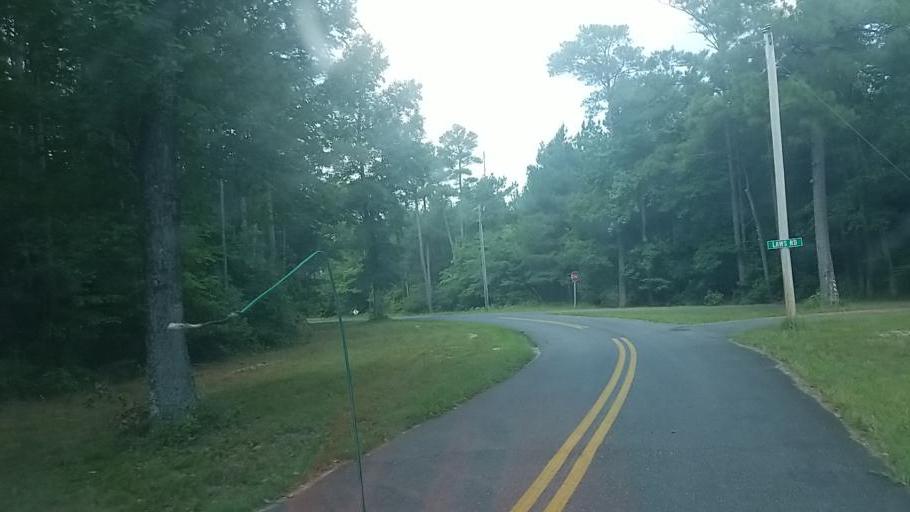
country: US
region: Maryland
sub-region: Worcester County
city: Snow Hill
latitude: 38.2550
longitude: -75.4373
